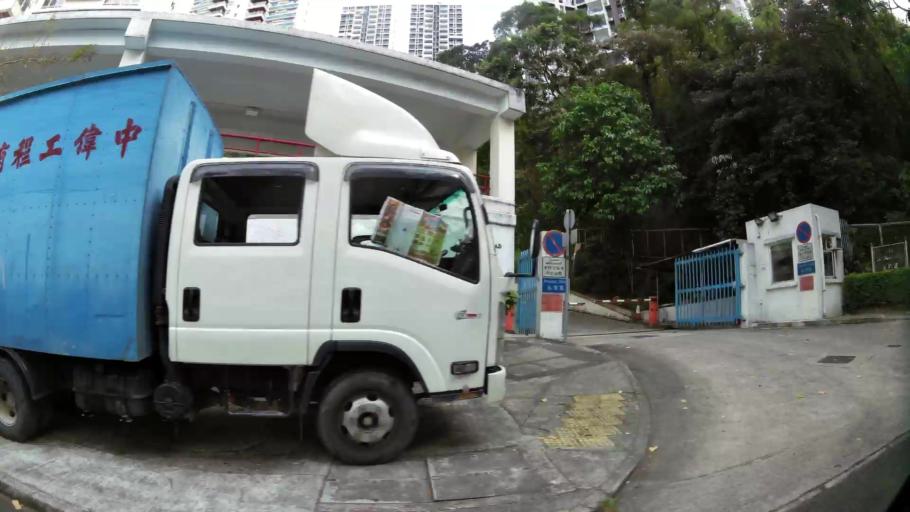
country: HK
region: Wanchai
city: Wan Chai
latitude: 22.2715
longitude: 114.1921
